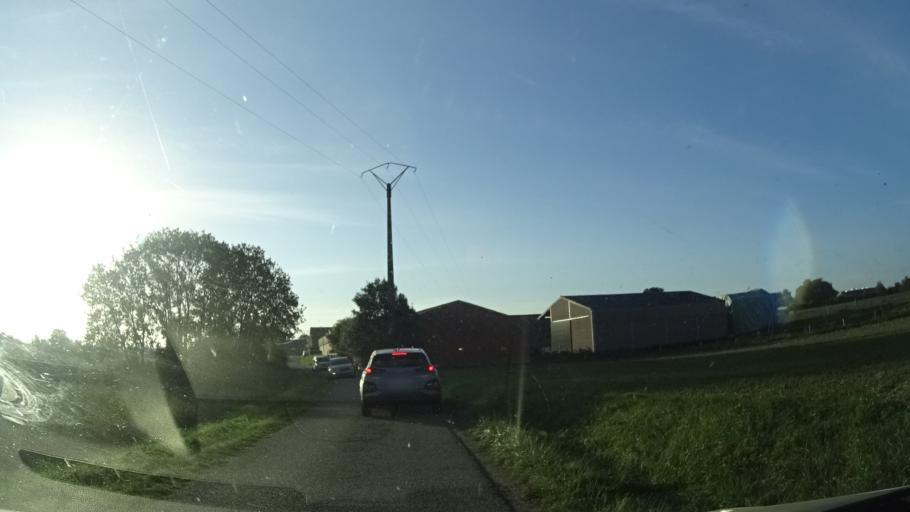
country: BE
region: Wallonia
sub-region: Province du Hainaut
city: Beaumont
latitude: 50.2517
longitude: 4.2555
